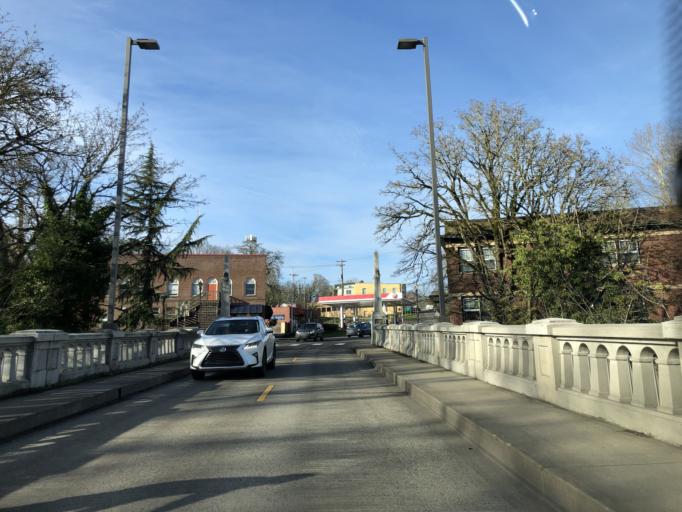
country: US
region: Oregon
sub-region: Clackamas County
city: Oregon City
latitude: 45.3595
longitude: -122.6101
